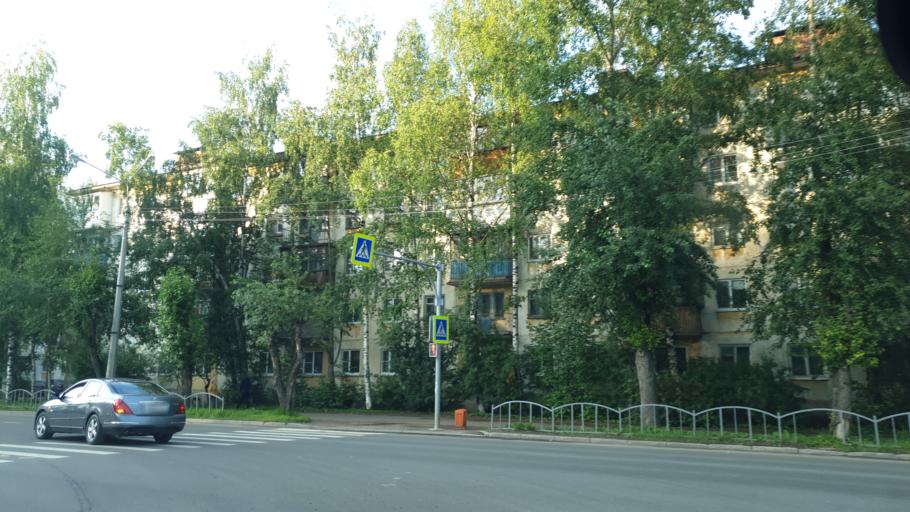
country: RU
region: Komi Republic
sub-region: Syktyvdinskiy Rayon
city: Syktyvkar
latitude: 61.6671
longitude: 50.8126
